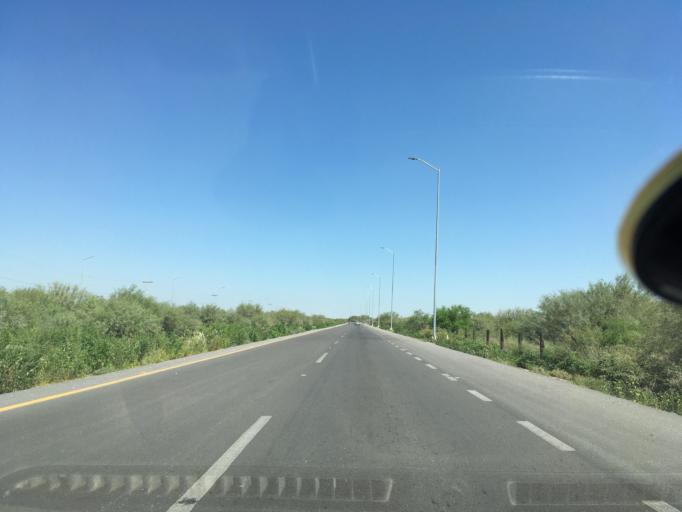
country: MX
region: Coahuila
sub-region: Torreon
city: Fraccionamiento la Noria
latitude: 25.4827
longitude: -103.3193
